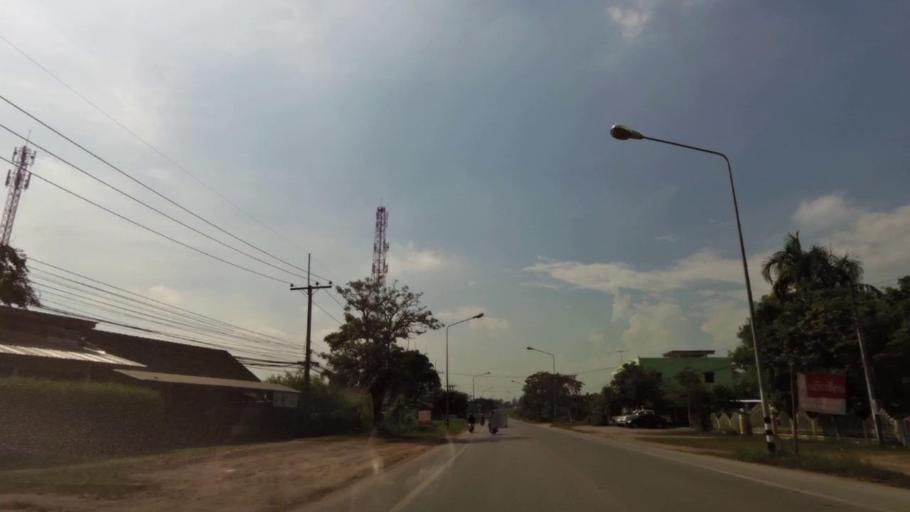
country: TH
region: Chiang Rai
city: Chiang Rai
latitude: 19.8789
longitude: 99.7912
